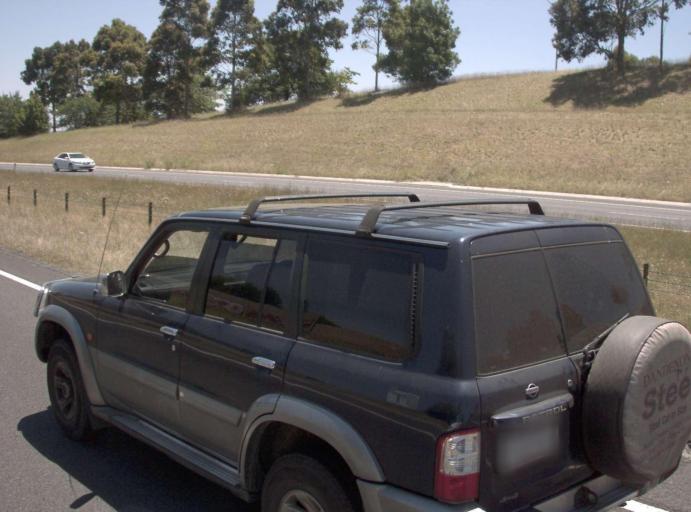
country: AU
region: Victoria
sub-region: Casey
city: Berwick
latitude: -38.0502
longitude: 145.3543
